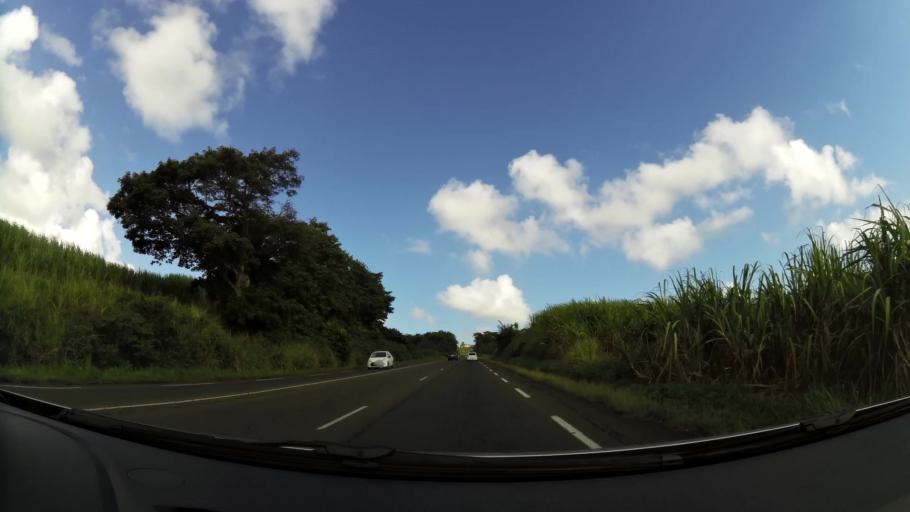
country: MQ
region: Martinique
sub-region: Martinique
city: Le Robert
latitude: 14.6941
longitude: -60.9411
